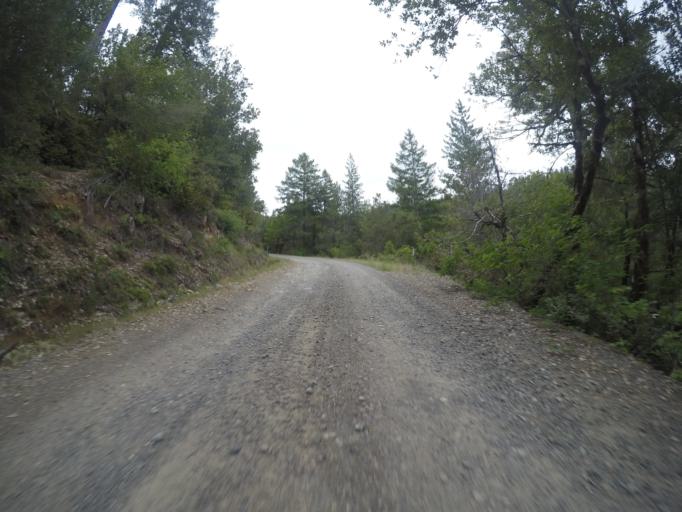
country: US
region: California
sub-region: Del Norte County
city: Bertsch-Oceanview
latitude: 41.7404
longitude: -123.8773
